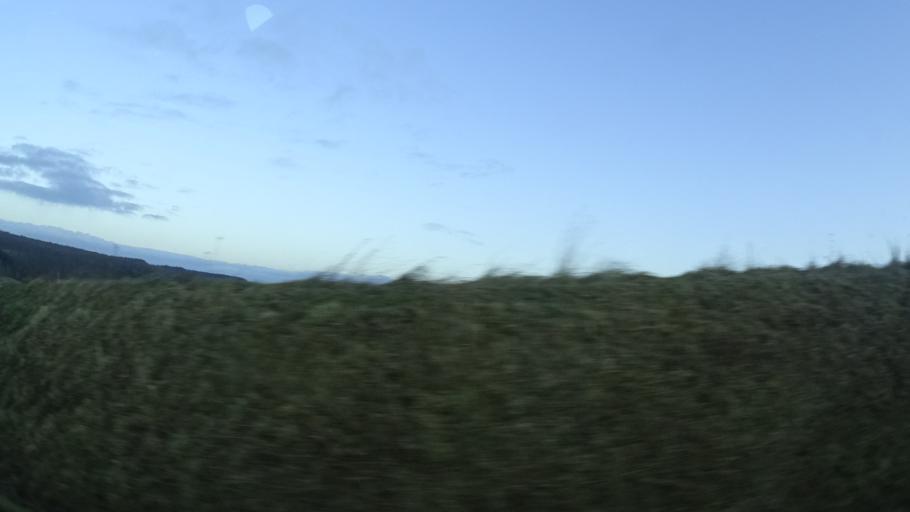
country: DE
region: Rheinland-Pfalz
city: Nieder-Wiesen
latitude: 49.7295
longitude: 7.9844
